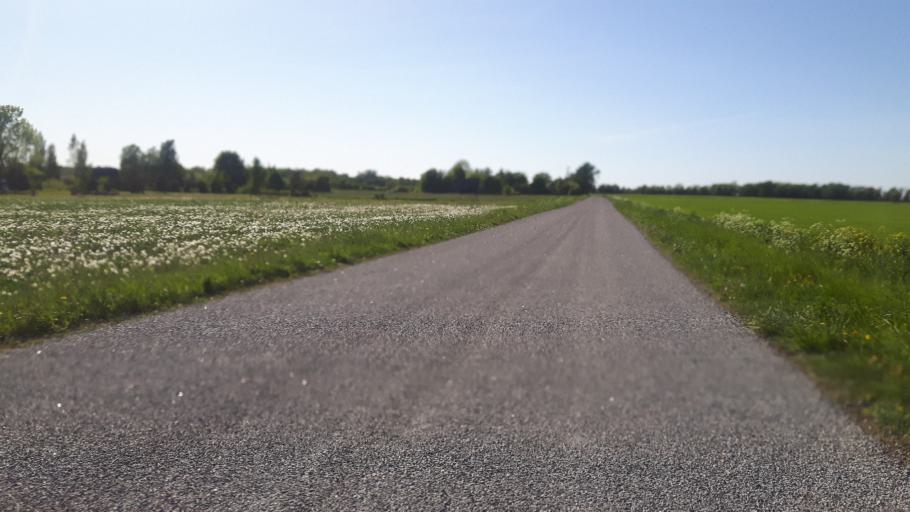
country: EE
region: Ida-Virumaa
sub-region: Kohtla-Jaerve linn
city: Kohtla-Jarve
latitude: 59.4356
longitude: 27.2024
